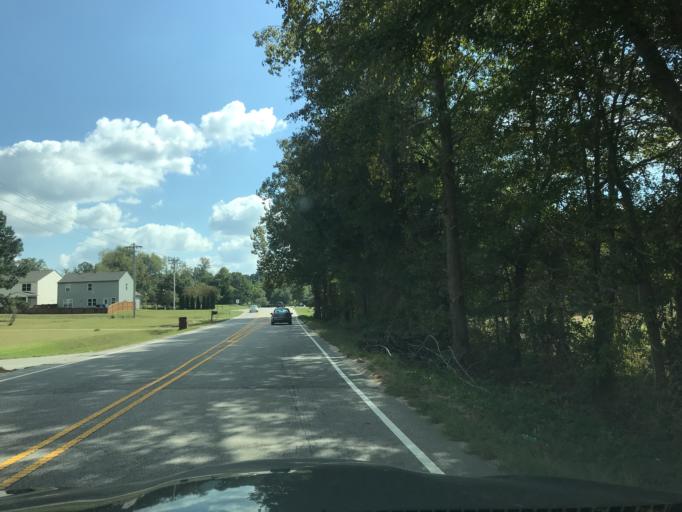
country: US
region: North Carolina
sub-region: Wake County
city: Rolesville
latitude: 35.8987
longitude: -78.5242
